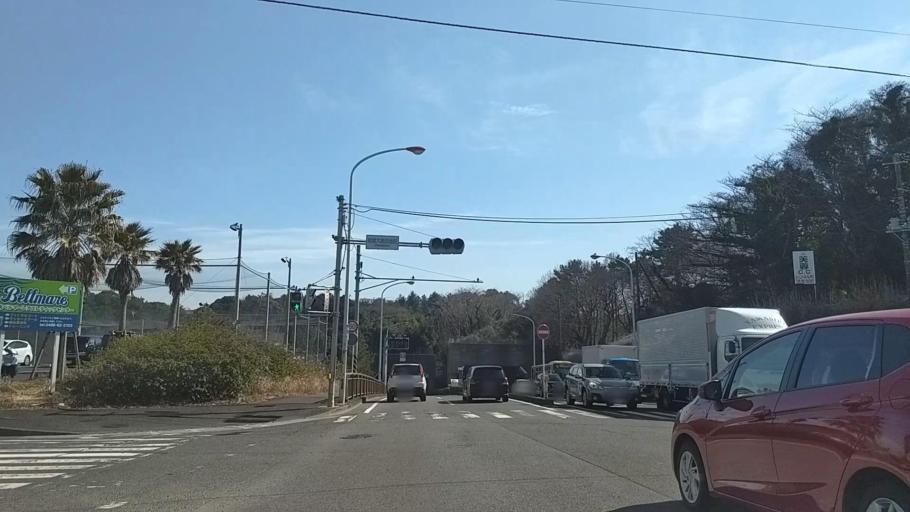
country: JP
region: Kanagawa
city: Fujisawa
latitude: 35.3532
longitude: 139.4439
